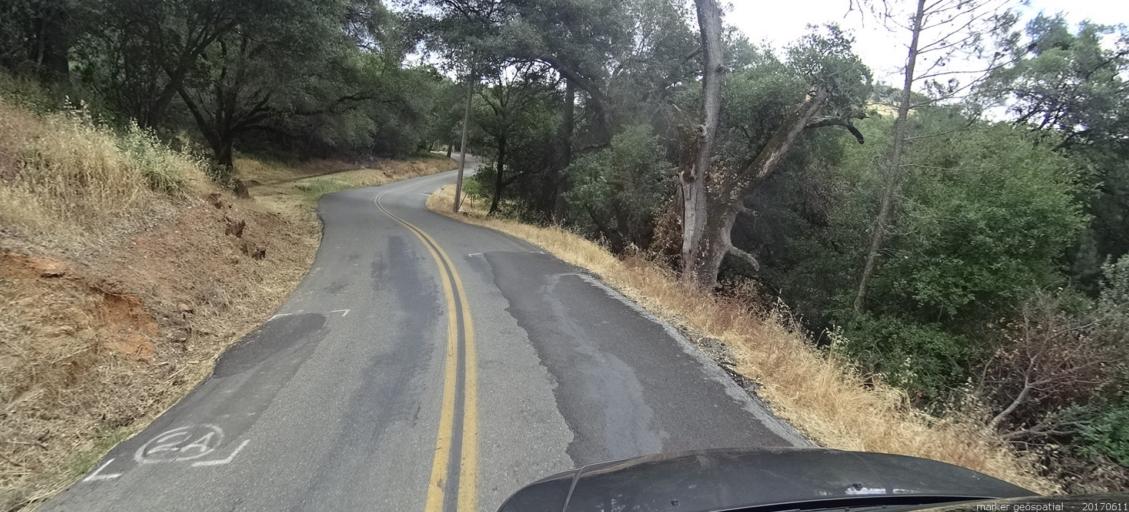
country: US
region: California
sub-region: Butte County
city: Oroville
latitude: 39.6429
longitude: -121.5450
